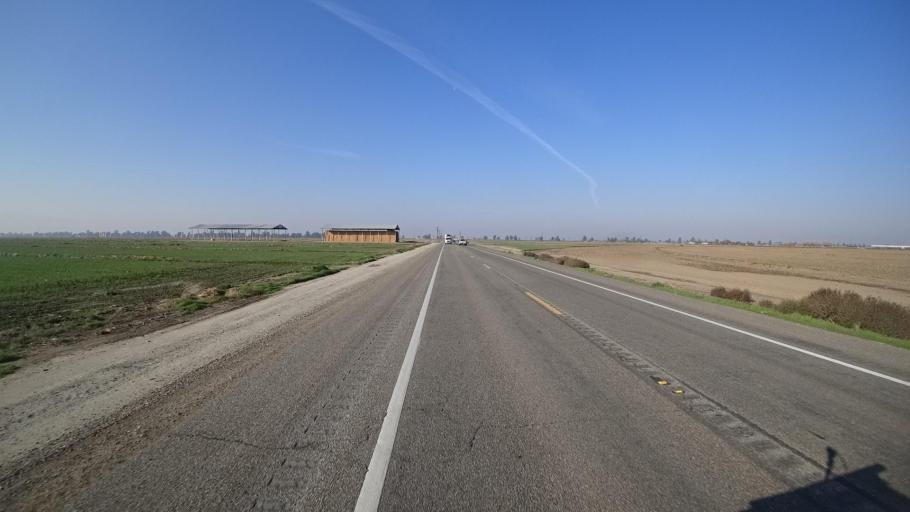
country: US
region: California
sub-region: Kern County
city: Greenfield
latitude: 35.2086
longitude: -118.9819
